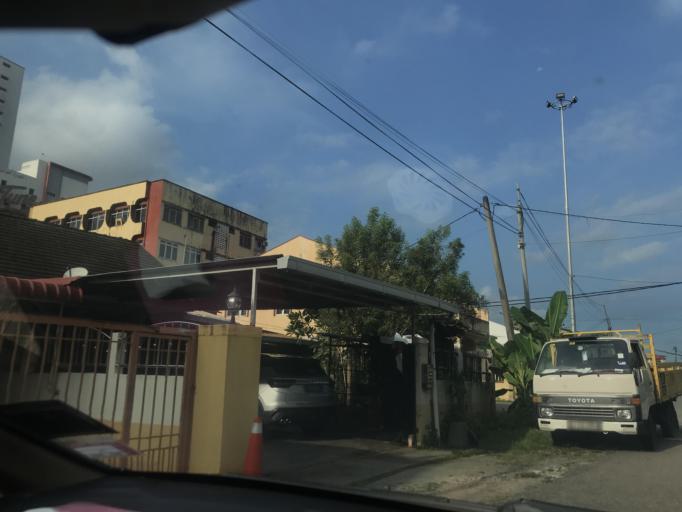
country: MY
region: Kelantan
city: Kota Bharu
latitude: 6.1159
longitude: 102.2390
